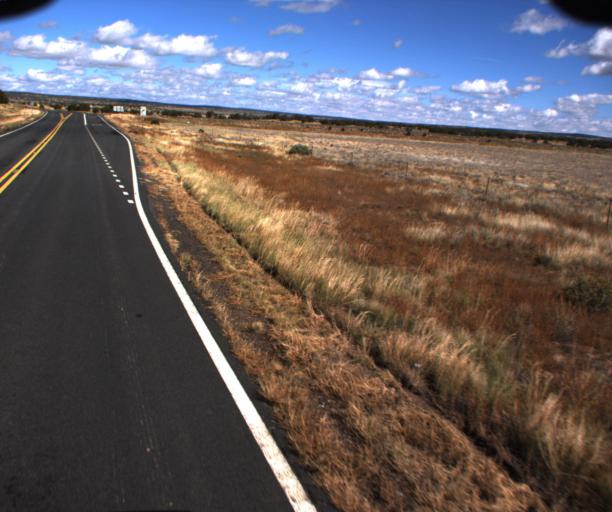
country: US
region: Arizona
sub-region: Apache County
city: Houck
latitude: 34.9980
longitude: -109.2272
